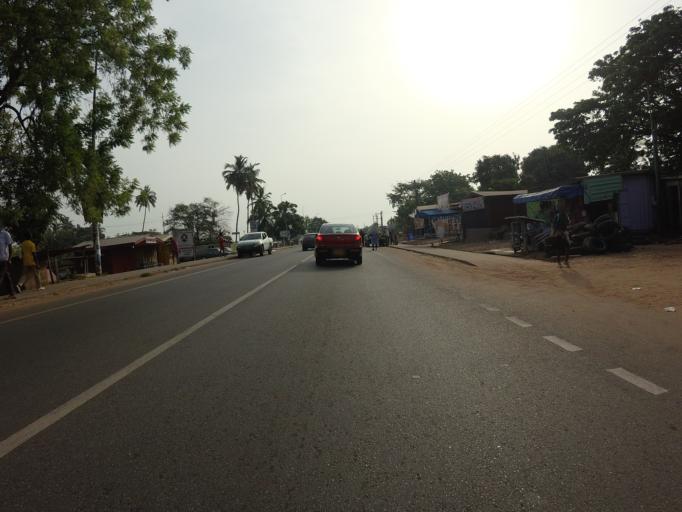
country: GH
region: Volta
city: Ho
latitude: 6.6044
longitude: 0.4770
